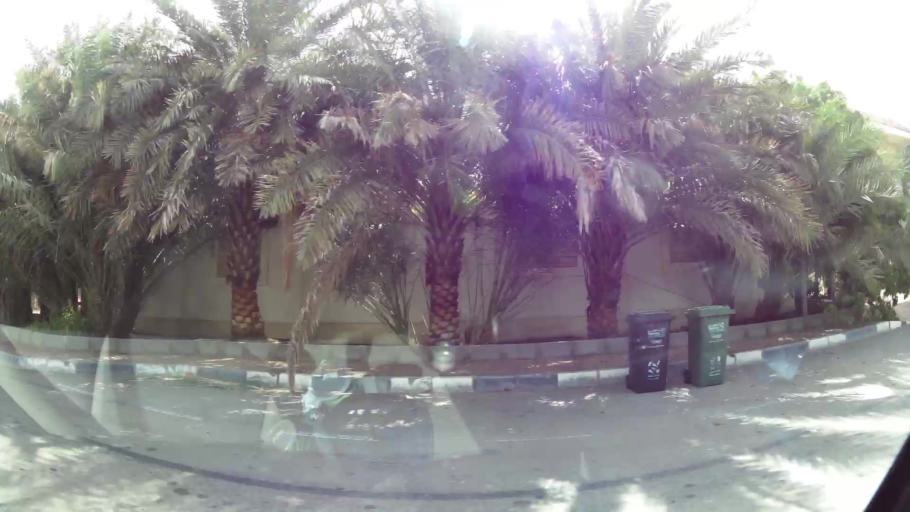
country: AE
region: Abu Dhabi
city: Al Ain
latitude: 24.1666
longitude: 55.6730
